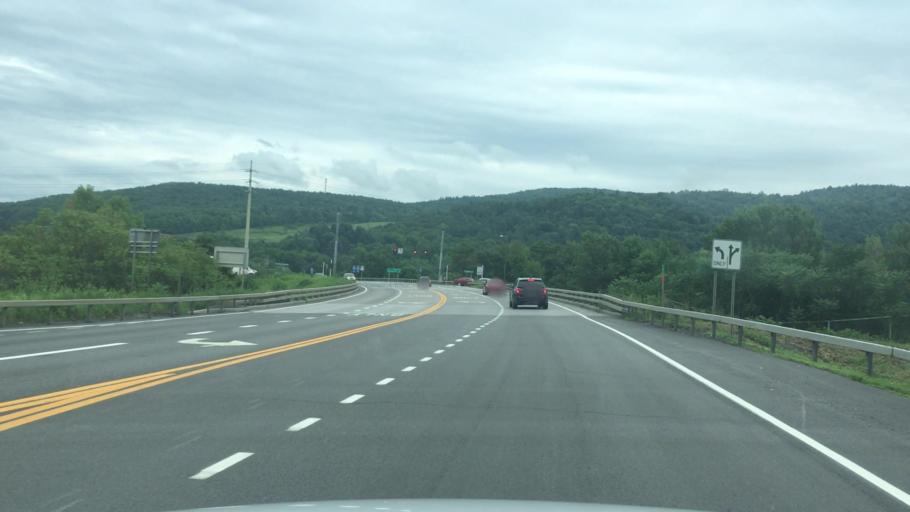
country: US
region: New York
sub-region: Otsego County
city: West End
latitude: 42.4422
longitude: -75.1074
